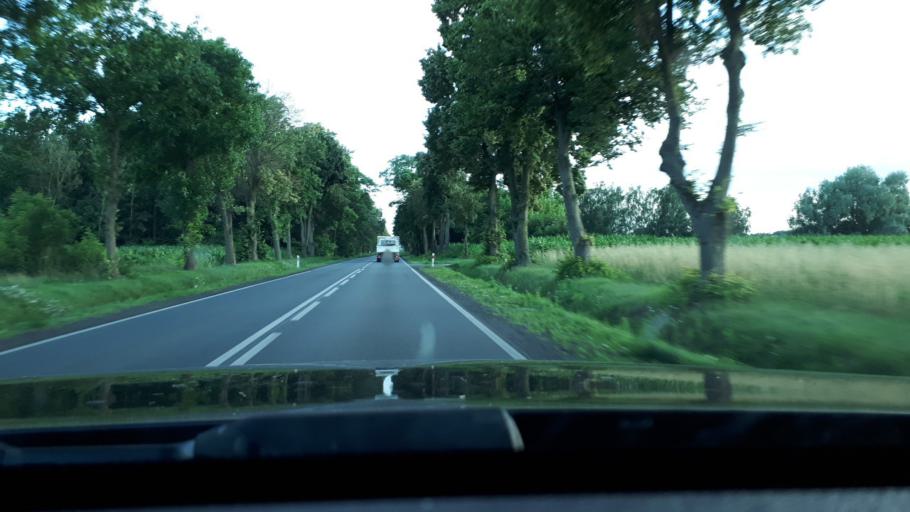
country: PL
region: Masovian Voivodeship
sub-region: Powiat ciechanowski
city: Ojrzen
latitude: 52.7417
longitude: 20.5243
